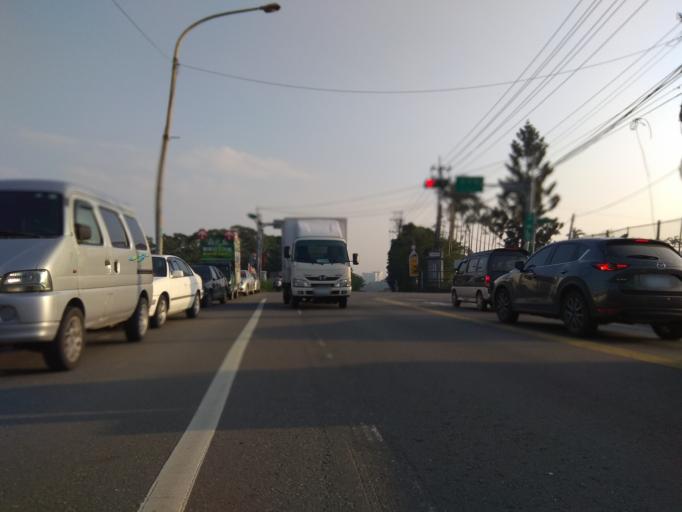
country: TW
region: Taiwan
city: Daxi
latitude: 24.9123
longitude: 121.1879
